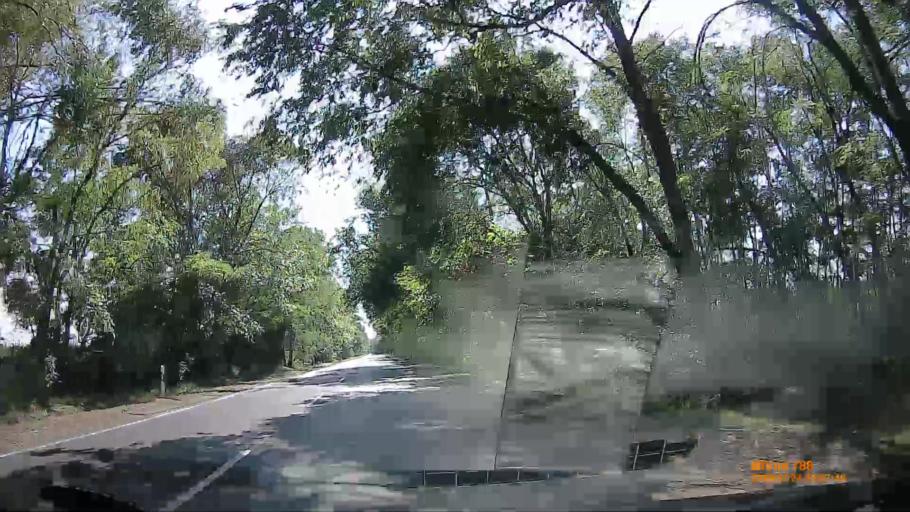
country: HU
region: Szabolcs-Szatmar-Bereg
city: Nyirmada
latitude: 48.0742
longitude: 22.2430
